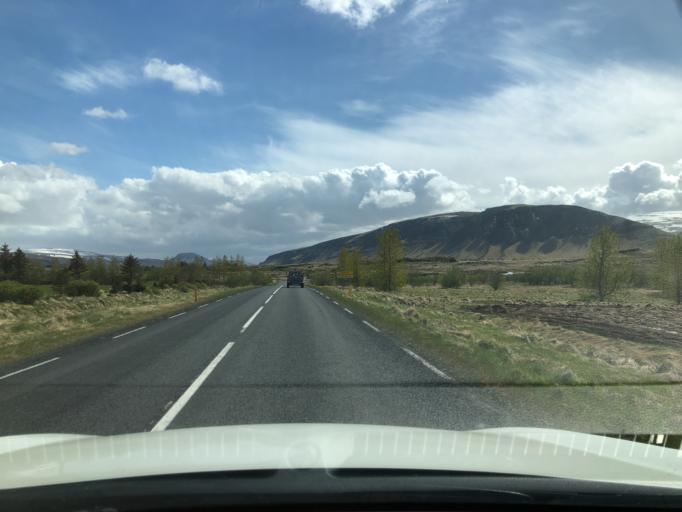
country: IS
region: Capital Region
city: Mosfellsbaer
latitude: 64.3441
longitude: -21.6128
